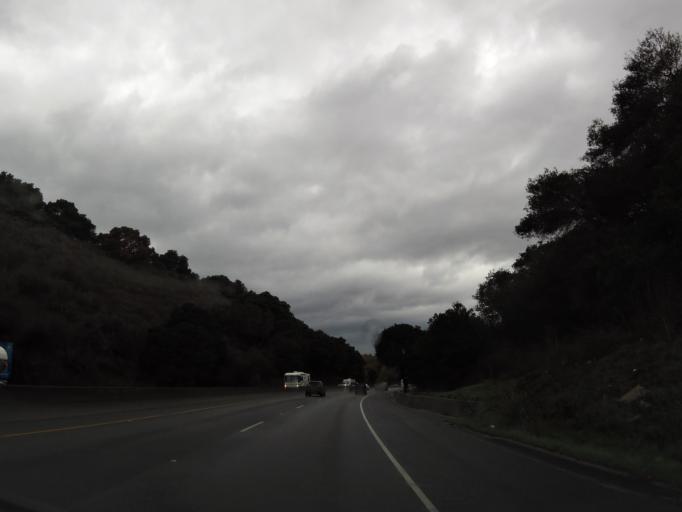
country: US
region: California
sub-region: San Benito County
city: Aromas
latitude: 36.8308
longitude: -121.6298
